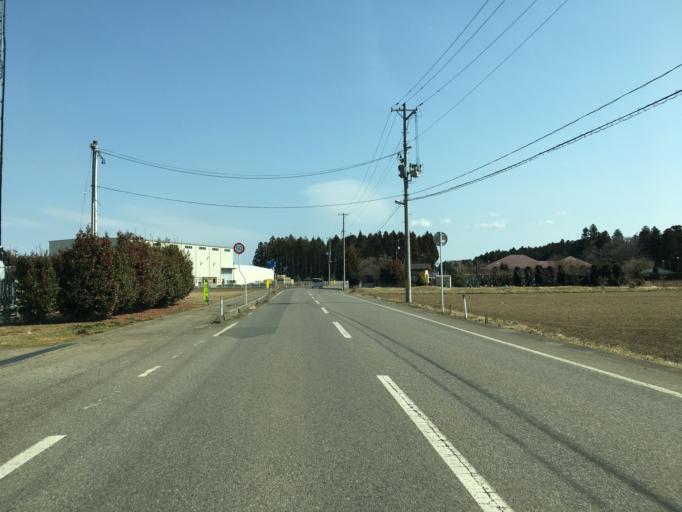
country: JP
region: Fukushima
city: Ishikawa
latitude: 37.1494
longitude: 140.3565
